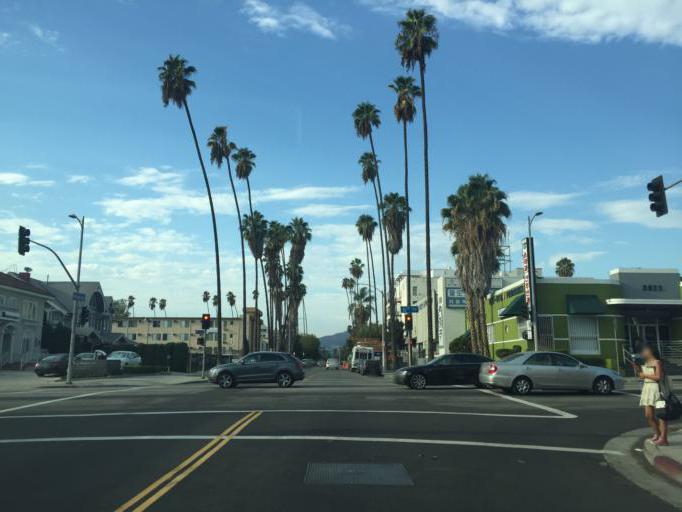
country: US
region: California
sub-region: Los Angeles County
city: Silver Lake
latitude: 34.0633
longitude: -118.3029
